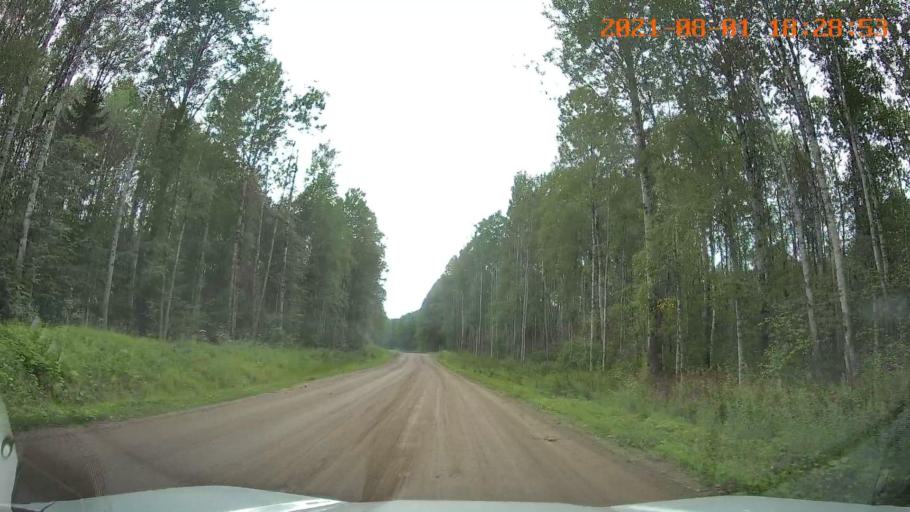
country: RU
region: Leningrad
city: Voznesen'ye
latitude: 60.8847
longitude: 35.3850
